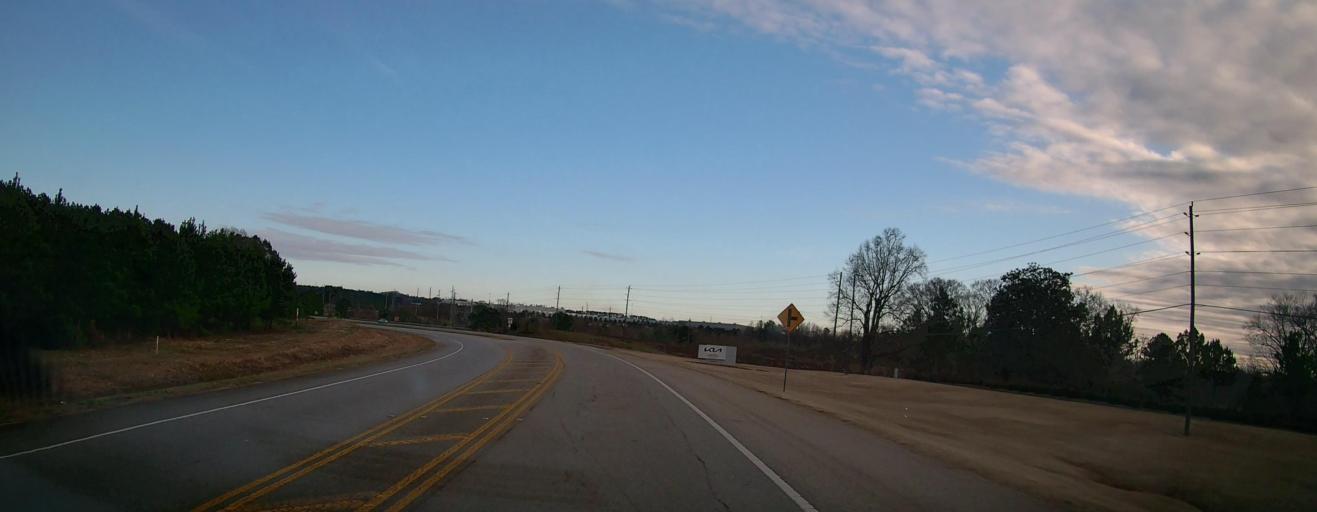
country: US
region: Georgia
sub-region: Troup County
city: West Point
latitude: 32.9339
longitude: -85.1270
